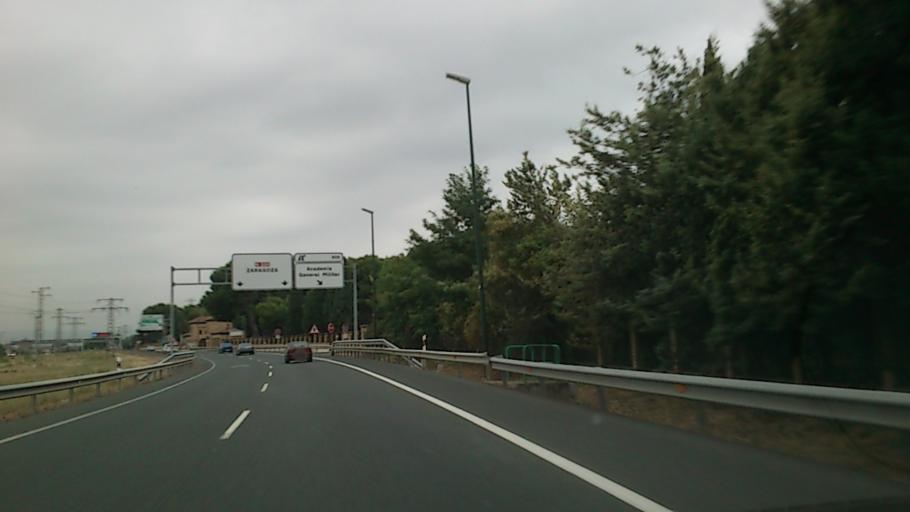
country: ES
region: Aragon
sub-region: Provincia de Zaragoza
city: Zaragoza
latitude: 41.7005
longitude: -0.8682
